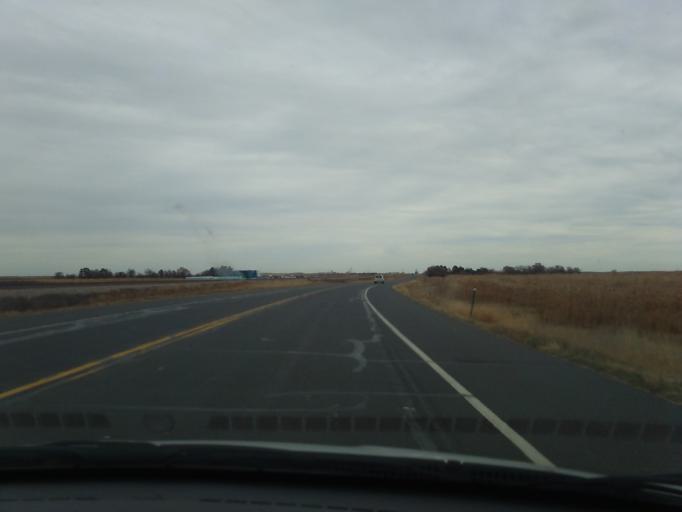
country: US
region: Colorado
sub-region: Yuma County
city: Yuma
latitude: 40.1187
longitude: -102.6557
